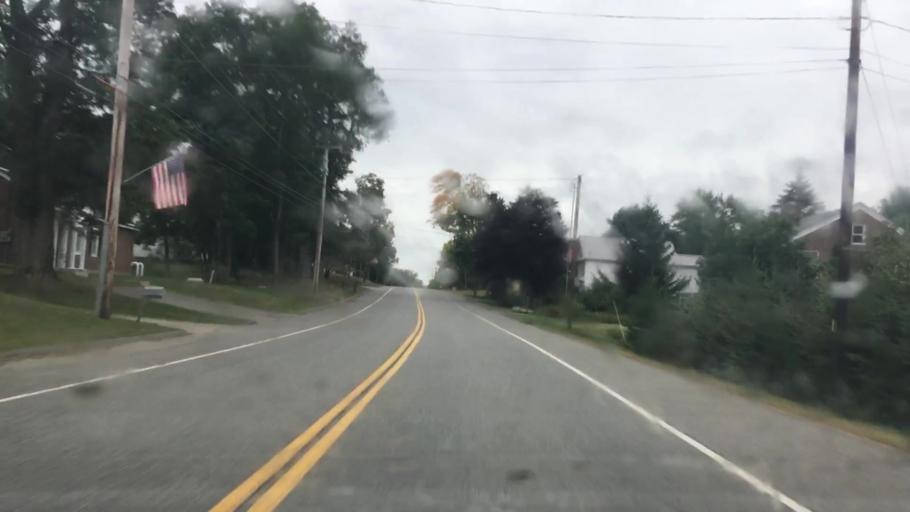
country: US
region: Maine
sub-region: Penobscot County
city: Orrington
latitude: 44.7291
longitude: -68.8274
